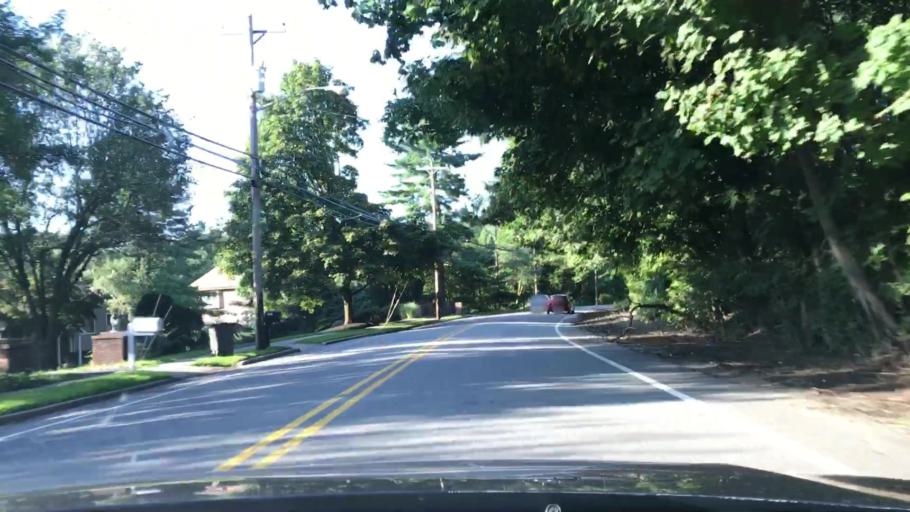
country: US
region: New Jersey
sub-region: Bergen County
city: Northvale
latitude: 40.9922
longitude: -73.9342
